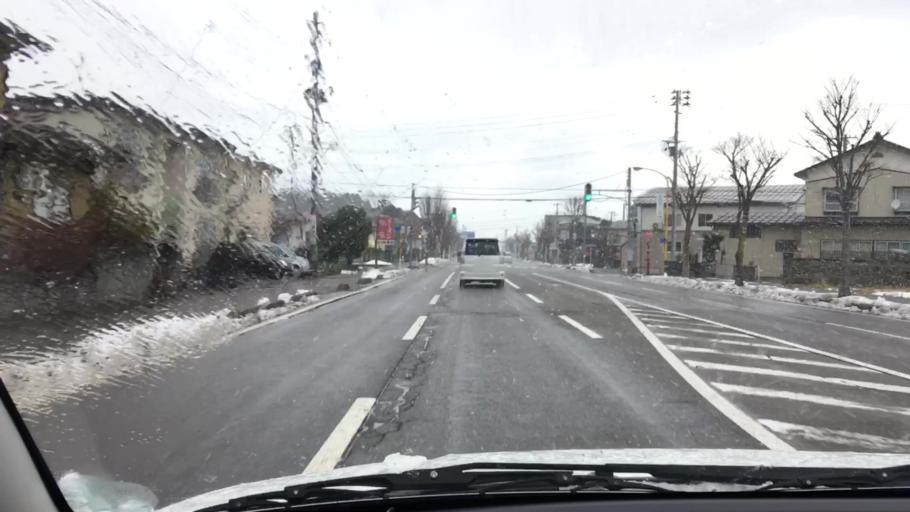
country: JP
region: Niigata
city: Joetsu
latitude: 37.1199
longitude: 138.2326
